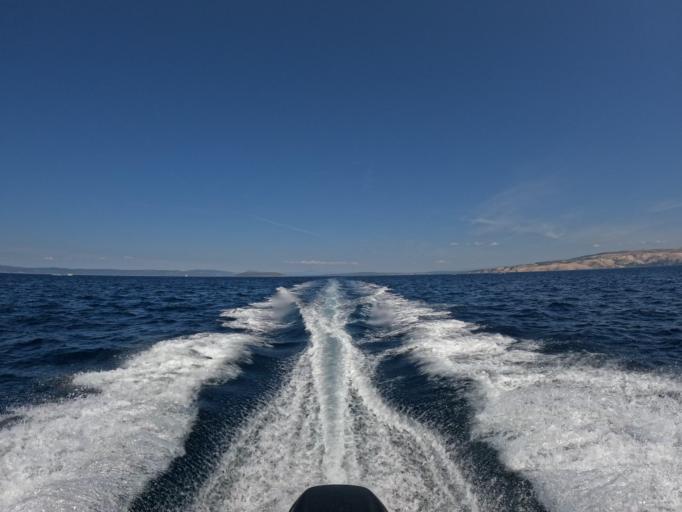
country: HR
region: Primorsko-Goranska
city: Punat
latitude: 44.9011
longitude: 14.6316
